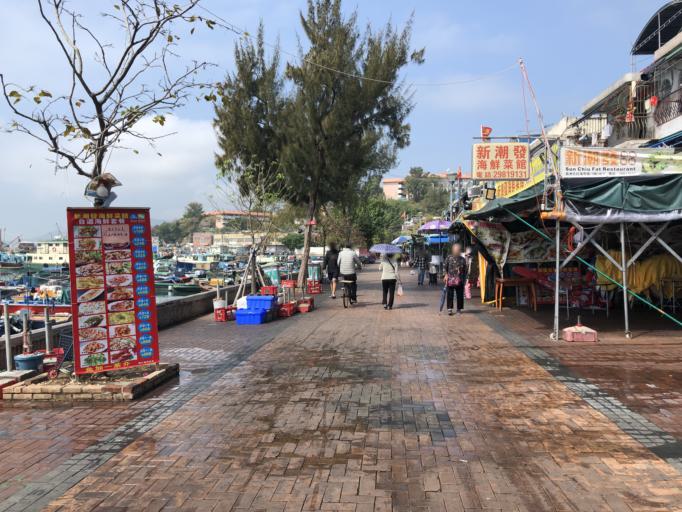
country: HK
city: Yung Shue Wan
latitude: 22.2110
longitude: 114.0276
